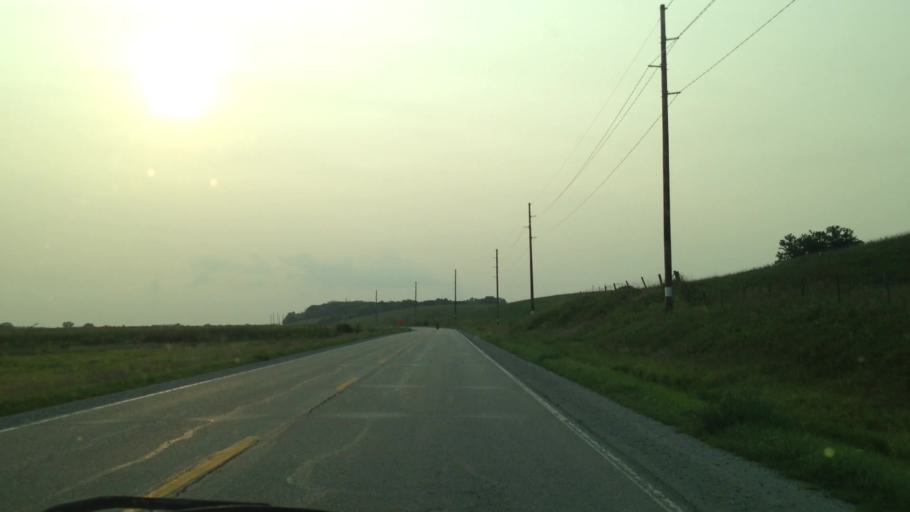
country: US
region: Iowa
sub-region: Benton County
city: Walford
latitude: 41.7965
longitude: -91.9138
